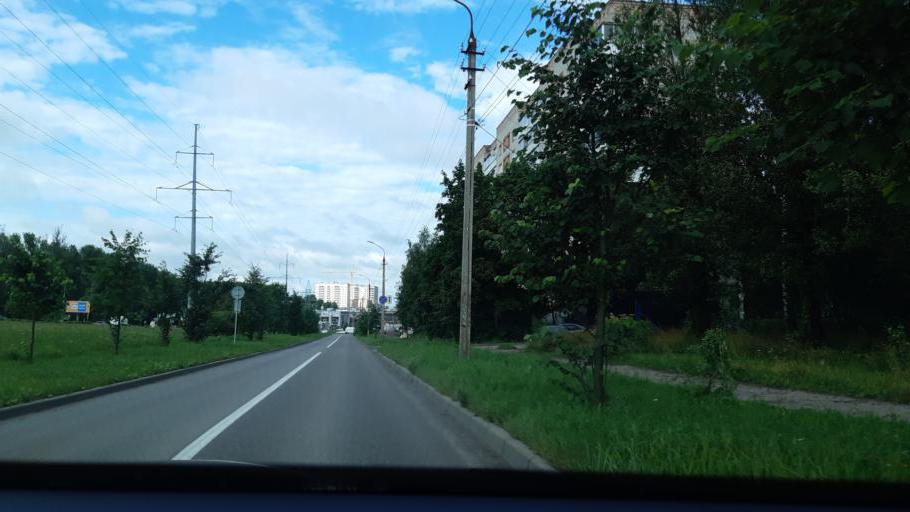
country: RU
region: Smolensk
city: Smolensk
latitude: 54.7627
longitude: 32.0868
